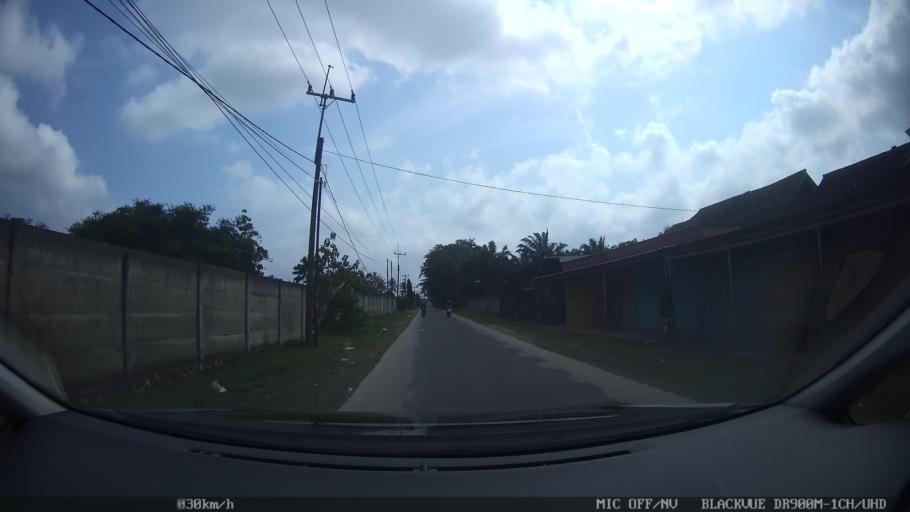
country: ID
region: Lampung
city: Kedaton
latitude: -5.3366
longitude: 105.2772
